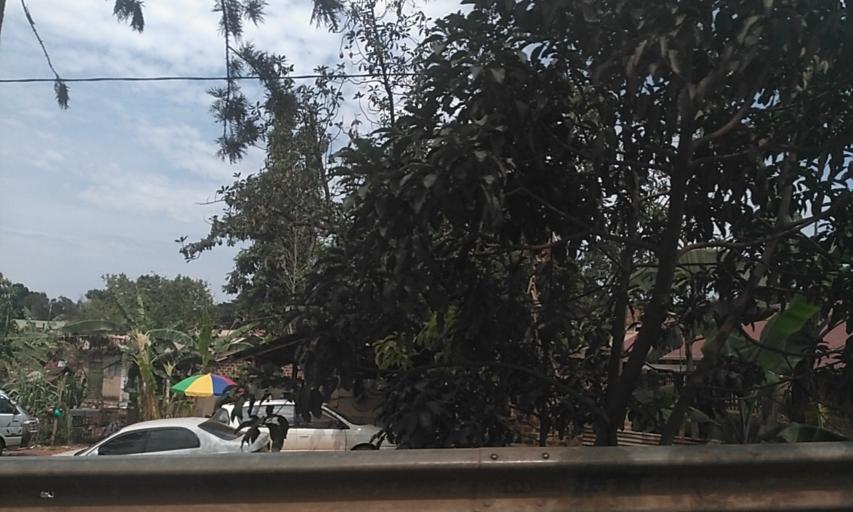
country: UG
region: Central Region
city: Kampala Central Division
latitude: 0.3038
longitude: 32.5445
